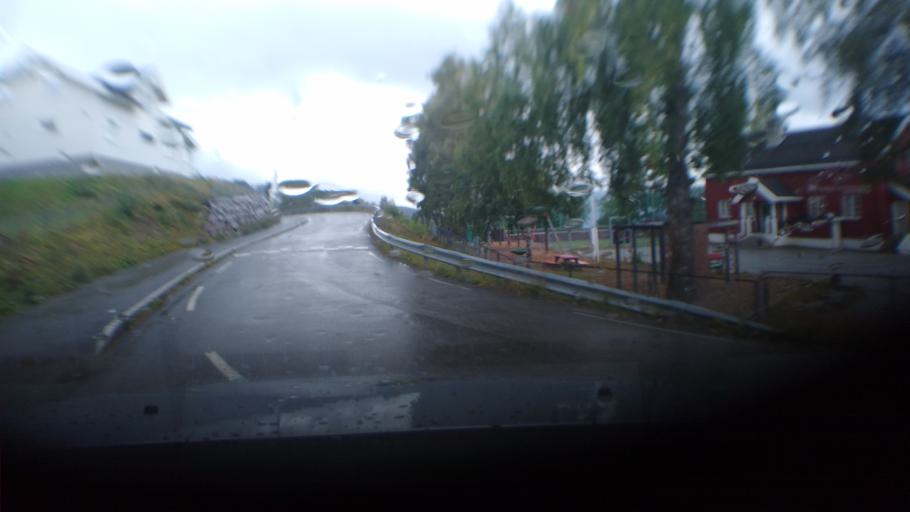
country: NO
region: Oppland
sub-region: Ringebu
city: Ringebu
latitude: 61.5942
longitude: 10.0501
